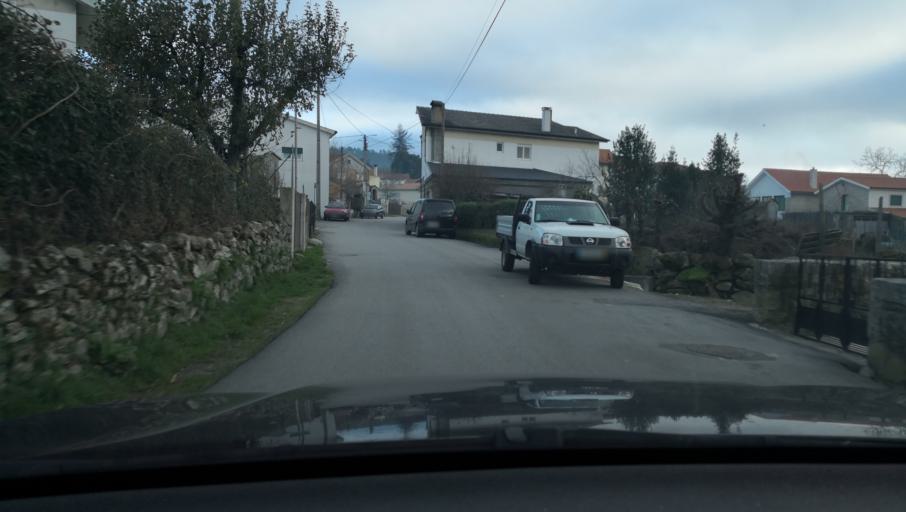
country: PT
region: Vila Real
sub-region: Vila Real
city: Vila Real
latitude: 41.3380
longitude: -7.6635
